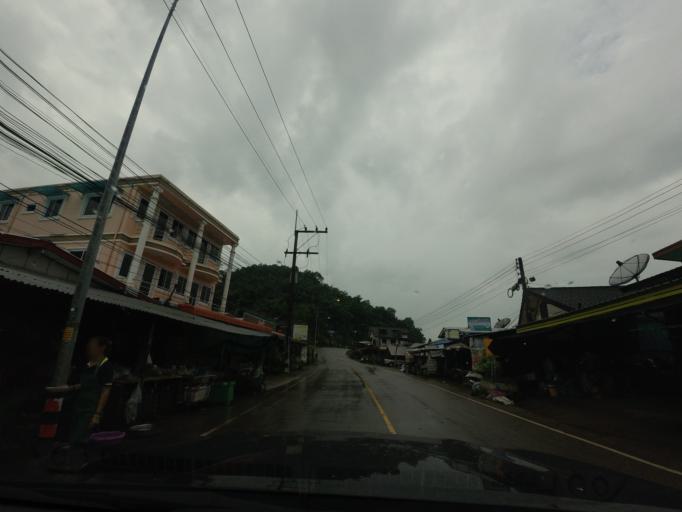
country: TH
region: Nong Khai
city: Sangkhom
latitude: 18.2073
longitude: 102.1288
